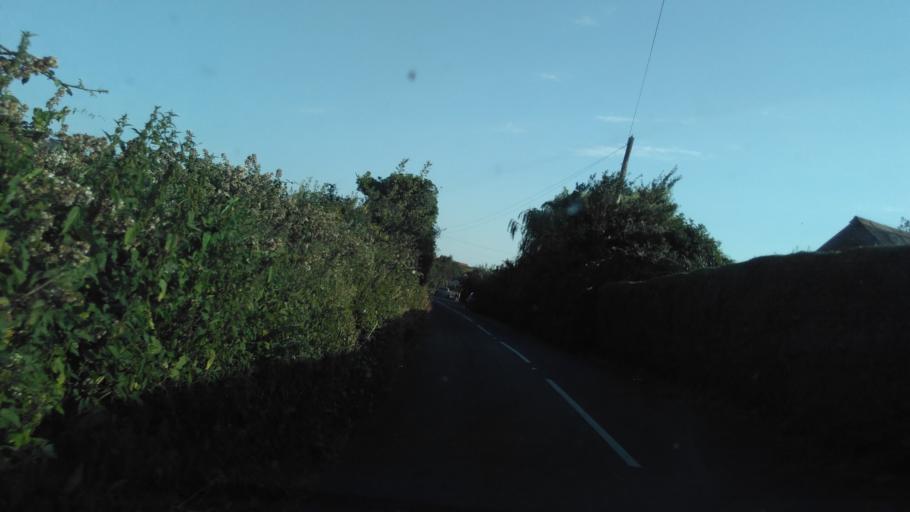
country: GB
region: England
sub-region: Kent
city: Whitstable
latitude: 51.3413
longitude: 1.0007
